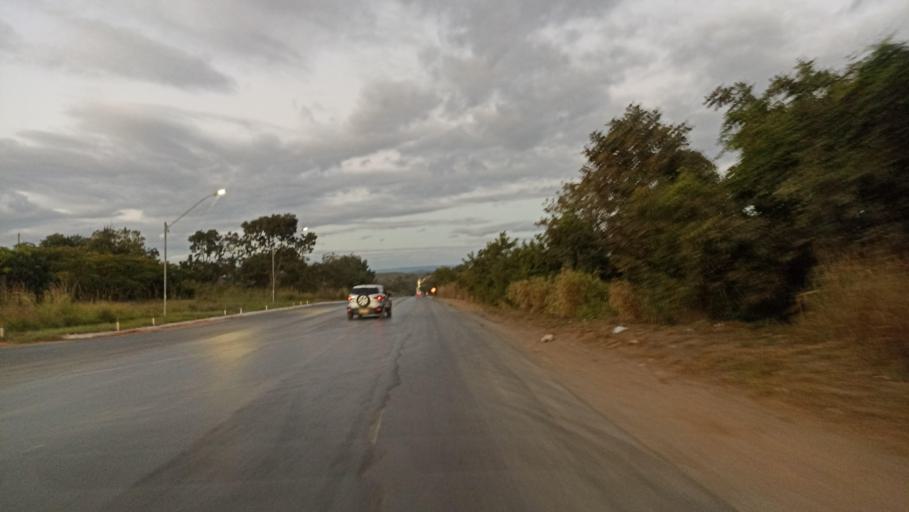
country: BR
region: Minas Gerais
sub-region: Montes Claros
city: Montes Claros
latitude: -16.6590
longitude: -43.7389
